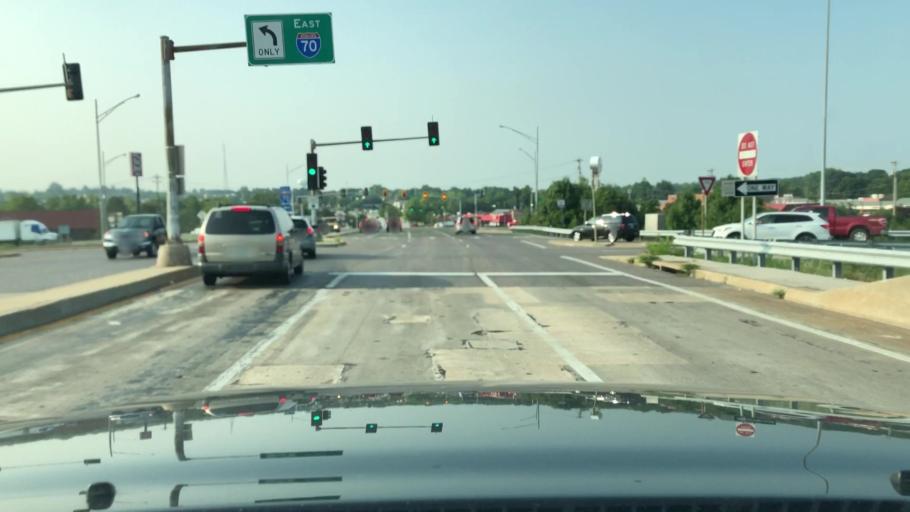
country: US
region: Missouri
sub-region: Saint Charles County
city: Saint Charles
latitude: 38.7864
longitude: -90.5331
